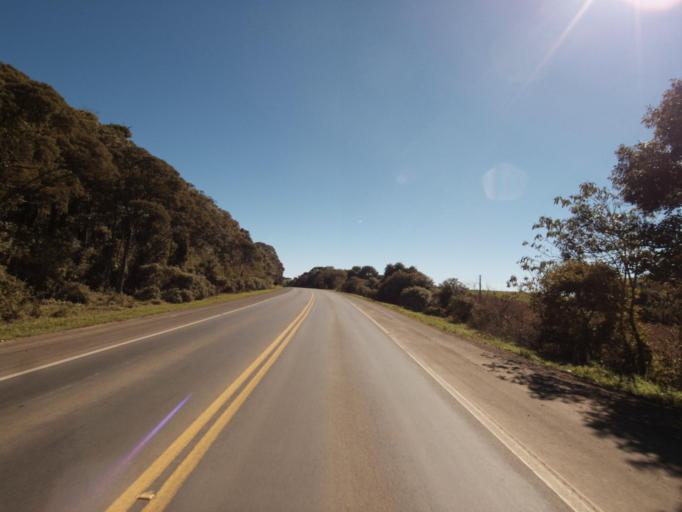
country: BR
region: Santa Catarina
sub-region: Xanxere
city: Xanxere
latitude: -26.8700
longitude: -52.1989
